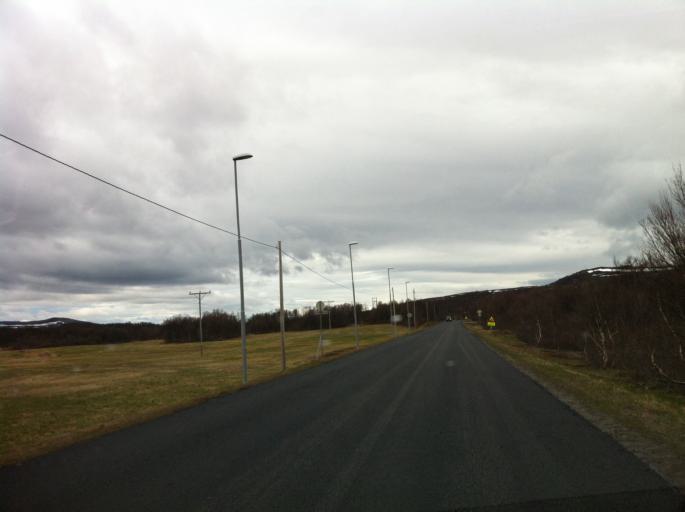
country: NO
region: Sor-Trondelag
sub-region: Tydal
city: Aas
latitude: 62.6402
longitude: 12.0286
